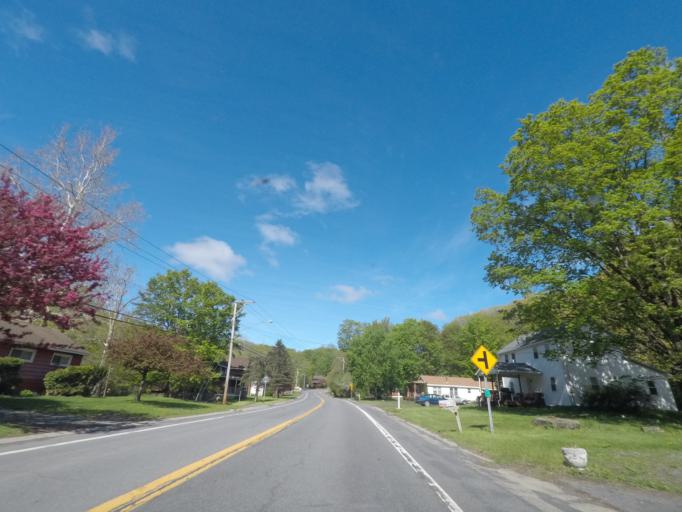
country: US
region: New York
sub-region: Albany County
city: Ravena
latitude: 42.4739
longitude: -73.9203
